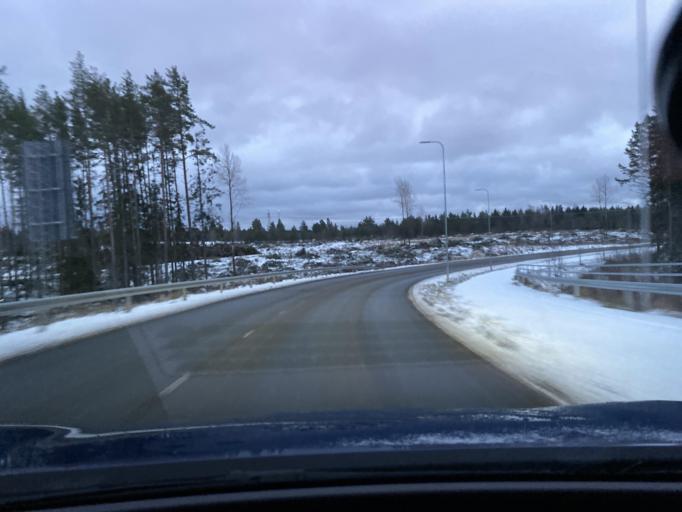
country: FI
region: Satakunta
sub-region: Rauma
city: Rauma
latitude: 61.1480
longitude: 21.5720
